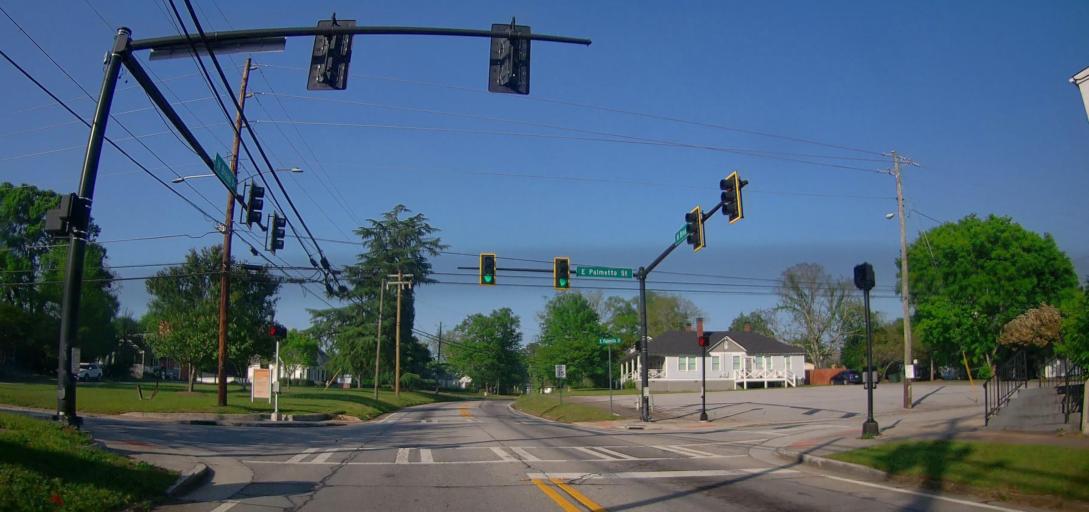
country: US
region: Georgia
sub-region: Newton County
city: Porterdale
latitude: 33.5749
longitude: -83.8942
